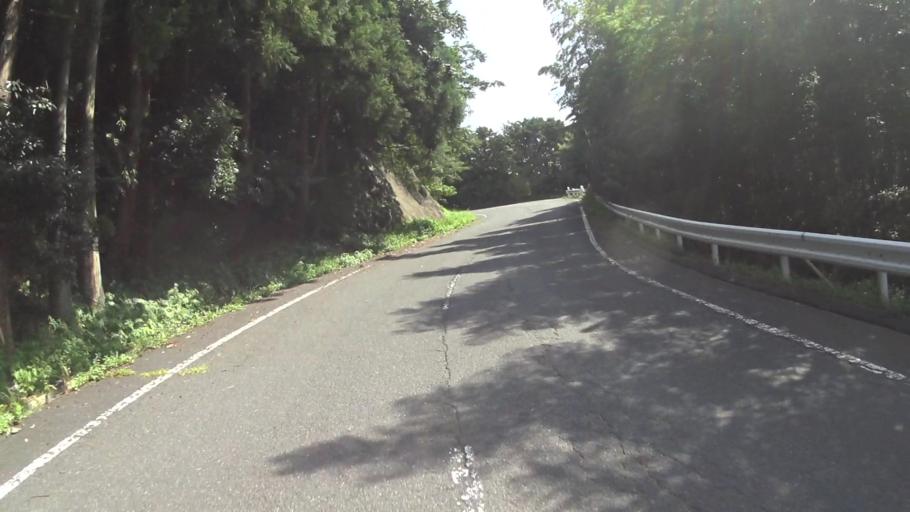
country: JP
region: Kyoto
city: Miyazu
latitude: 35.6742
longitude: 135.2455
